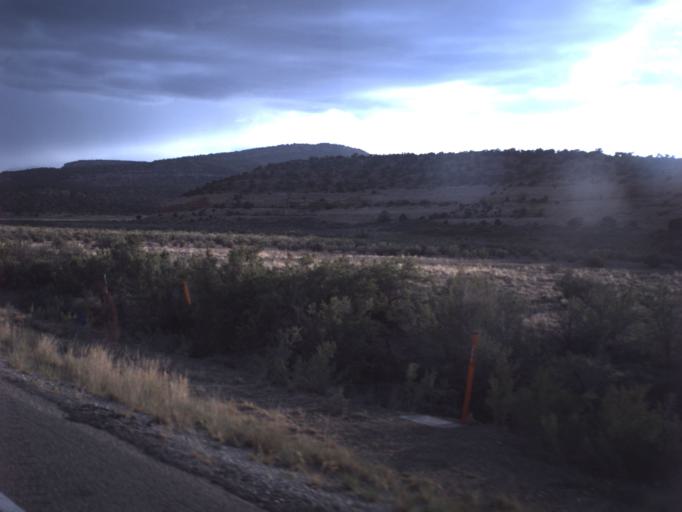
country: US
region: Utah
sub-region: San Juan County
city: Monticello
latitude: 38.0429
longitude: -109.3430
